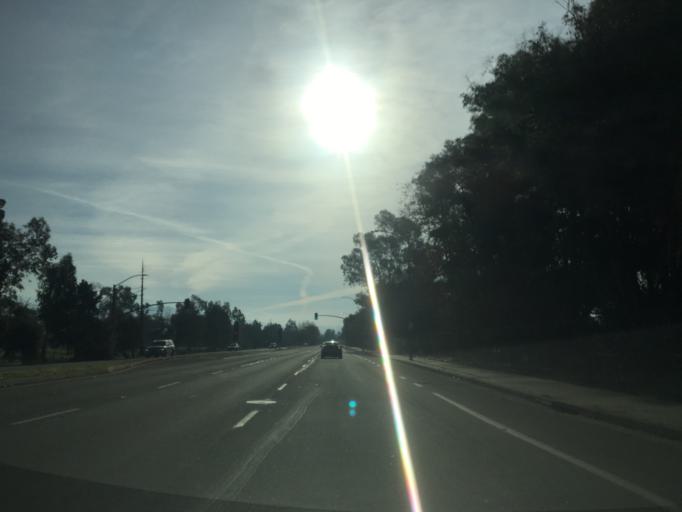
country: US
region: California
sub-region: Santa Clara County
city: Alum Rock
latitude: 37.3401
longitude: -121.8047
